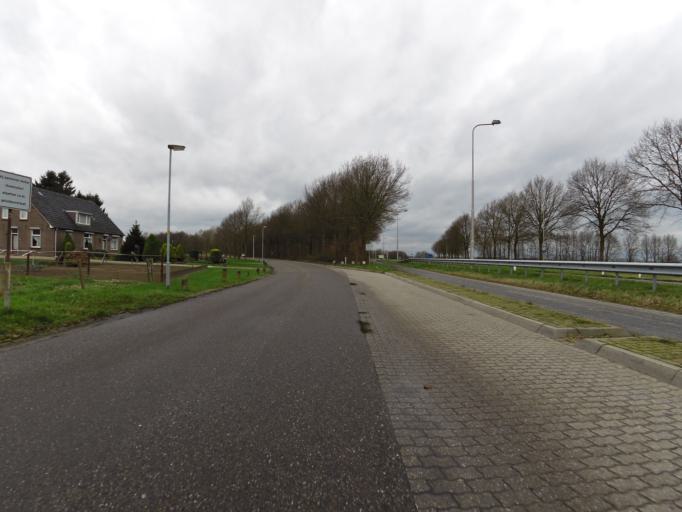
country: NL
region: Gelderland
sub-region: Gemeente Montferland
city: s-Heerenberg
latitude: 51.9137
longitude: 6.1688
